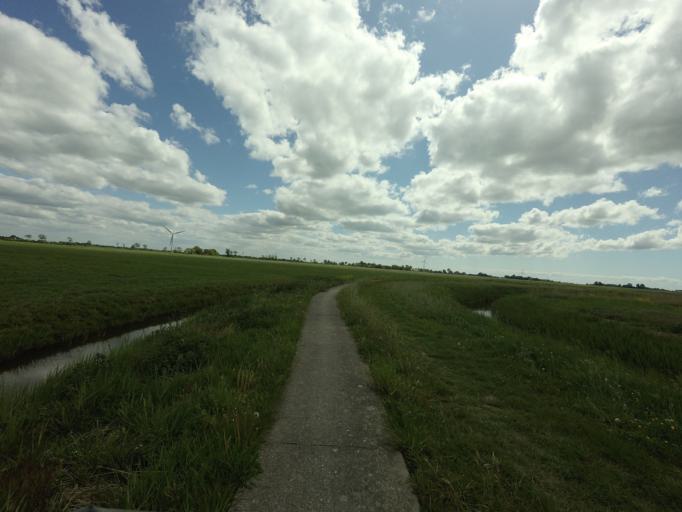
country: NL
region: Friesland
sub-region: Gemeente Littenseradiel
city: Wommels
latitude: 53.1315
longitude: 5.5733
